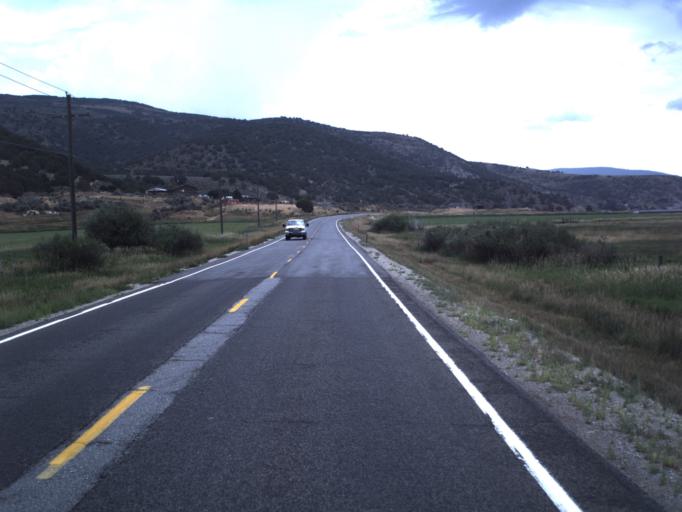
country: US
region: Utah
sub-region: Summit County
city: Oakley
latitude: 40.7501
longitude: -111.3682
